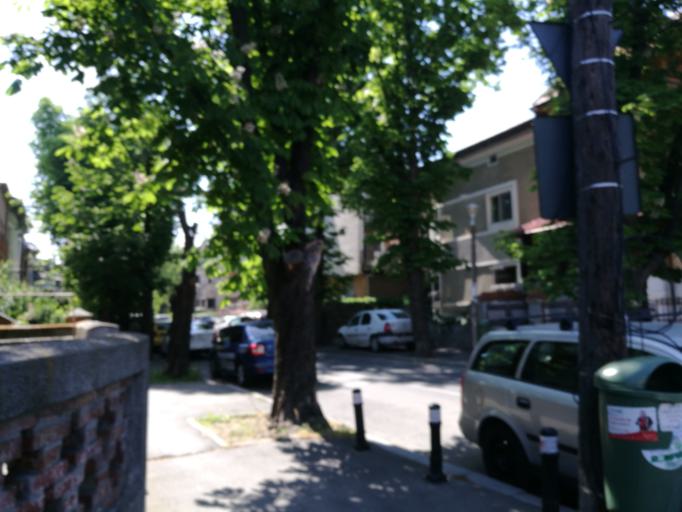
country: RO
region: Bucuresti
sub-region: Municipiul Bucuresti
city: Bucuresti
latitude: 44.4319
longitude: 26.0671
